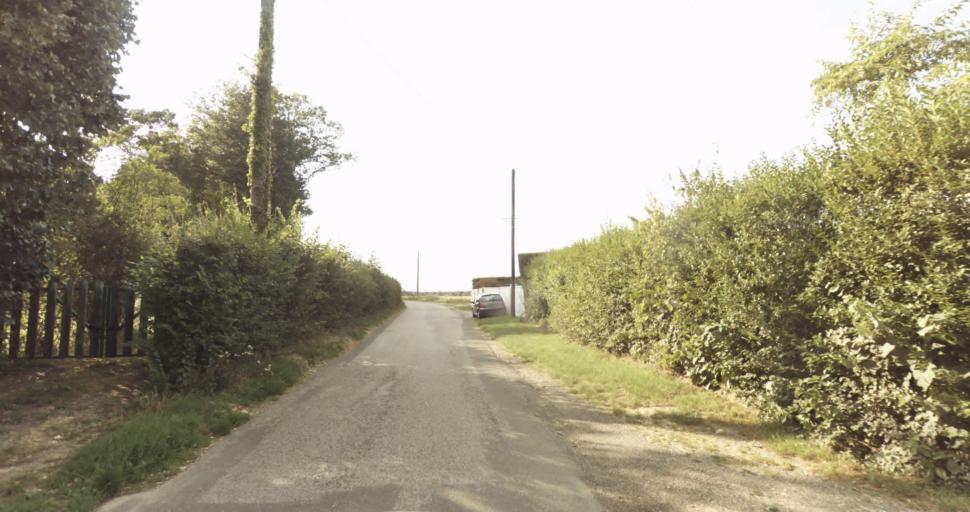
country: FR
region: Haute-Normandie
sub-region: Departement de l'Eure
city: La Couture-Boussey
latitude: 48.8934
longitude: 1.3739
